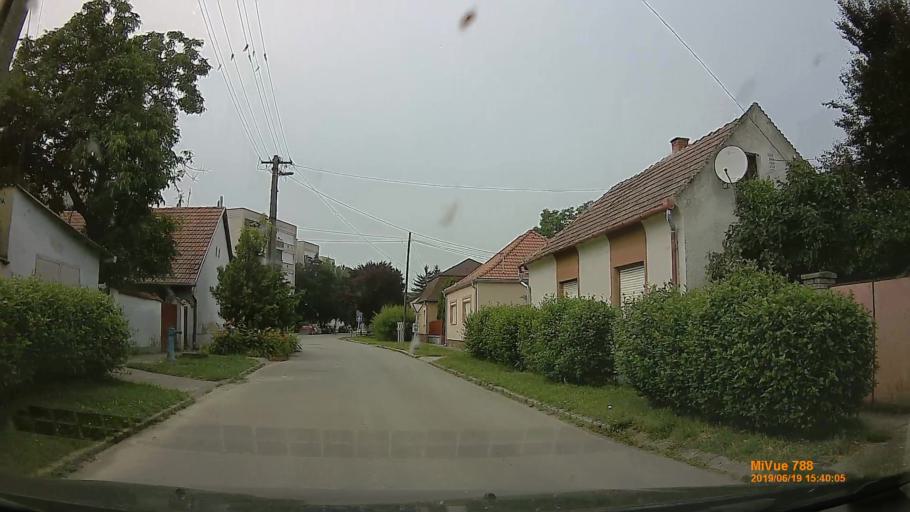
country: HU
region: Baranya
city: Szigetvar
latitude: 46.0461
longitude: 17.8062
